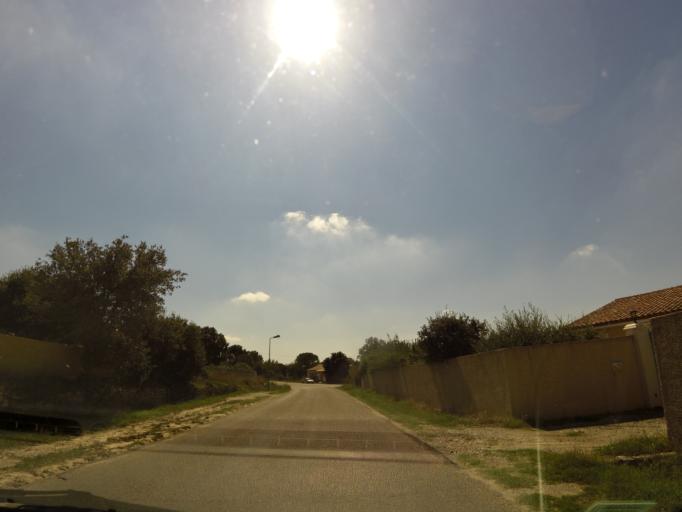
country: FR
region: Languedoc-Roussillon
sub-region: Departement du Gard
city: Villevieille
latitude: 43.7926
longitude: 4.1186
